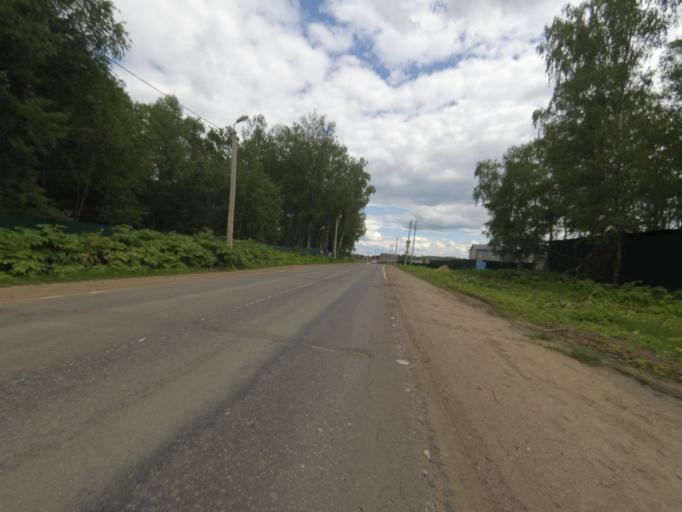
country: RU
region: Moskovskaya
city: Marfino
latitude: 56.0481
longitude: 37.5893
